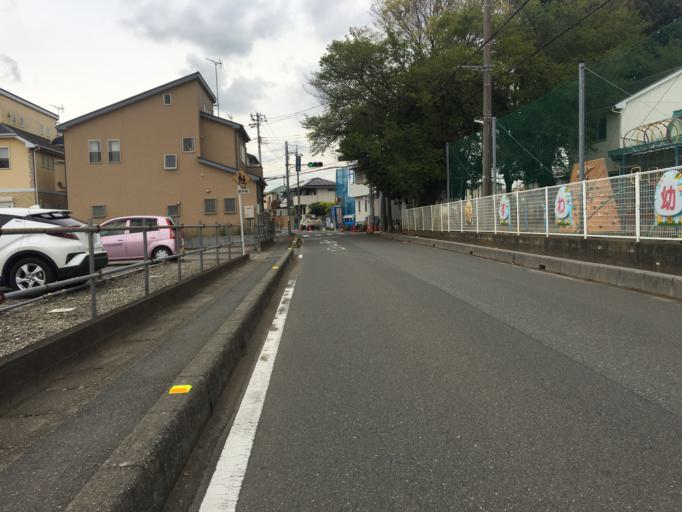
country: JP
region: Saitama
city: Oi
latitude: 35.8515
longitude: 139.5465
